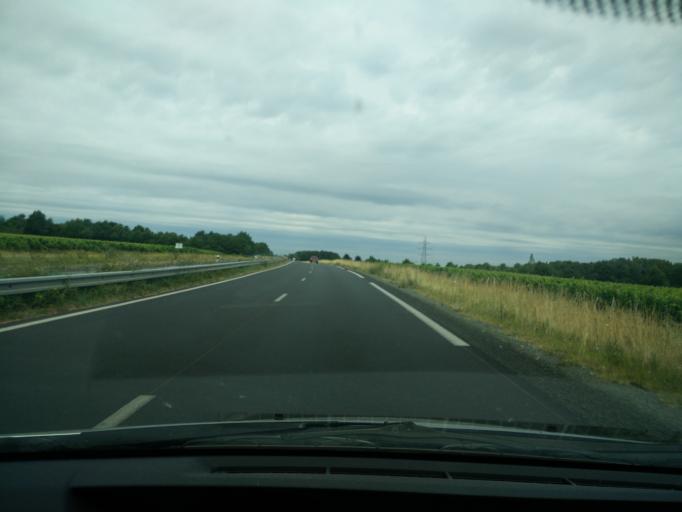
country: FR
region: Pays de la Loire
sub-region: Departement de Maine-et-Loire
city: Juigne-sur-Loire
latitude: 47.3812
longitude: -0.4762
